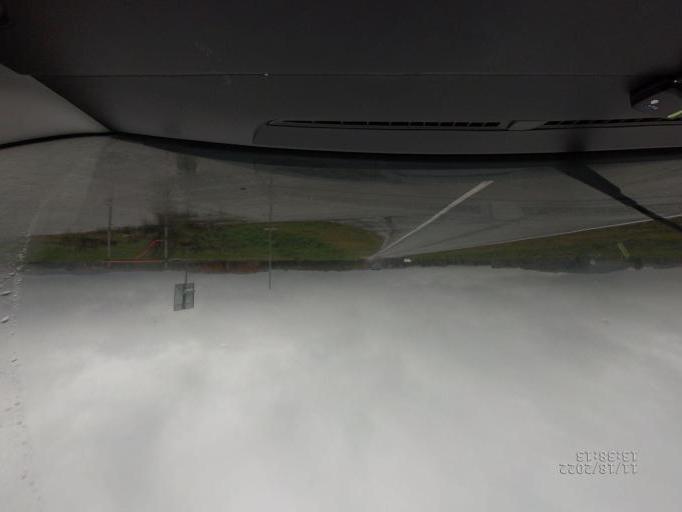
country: CZ
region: Plzensky
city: Kasejovice
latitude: 49.4306
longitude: 13.7890
